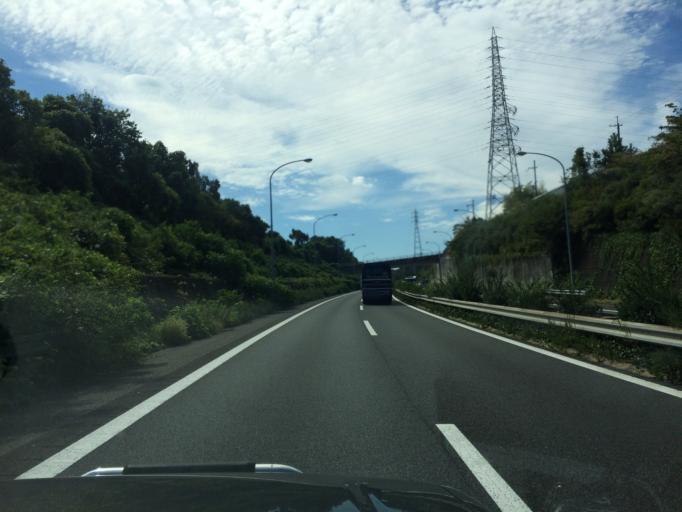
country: JP
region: Osaka
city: Izumi
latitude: 34.4485
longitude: 135.4453
